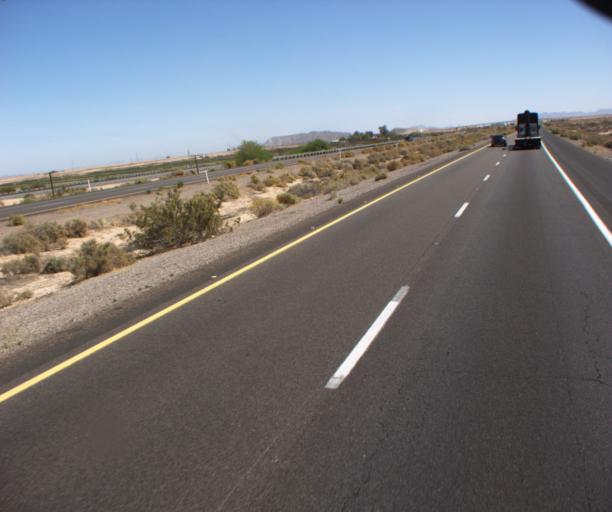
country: US
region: Arizona
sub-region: Yuma County
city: Wellton
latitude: 32.6726
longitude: -114.0927
